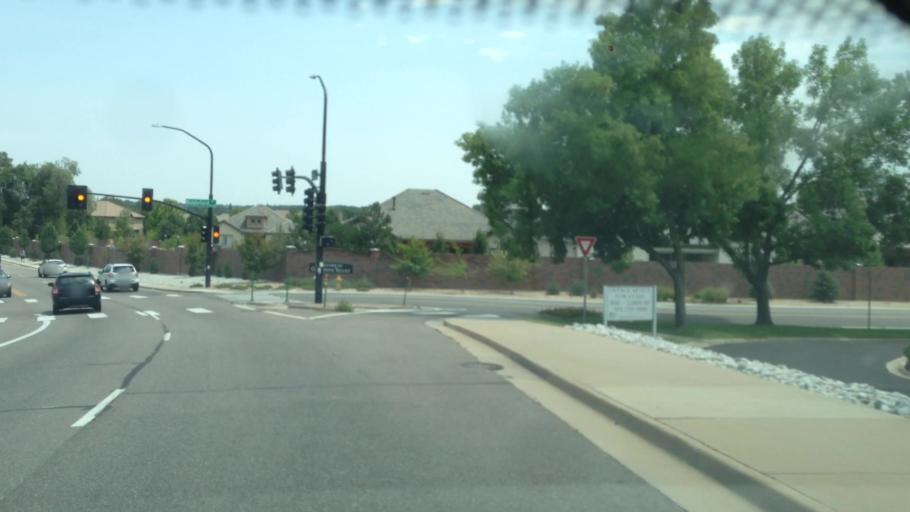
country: US
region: Colorado
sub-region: Arapahoe County
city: Columbine Valley
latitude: 39.6095
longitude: -105.0356
